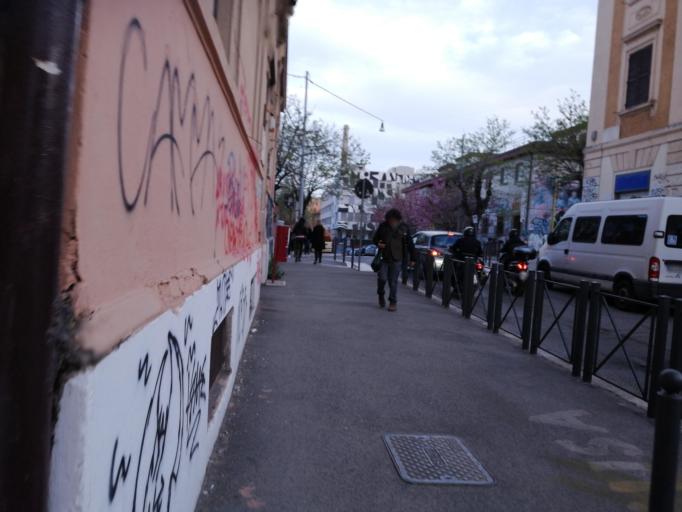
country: IT
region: Latium
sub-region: Citta metropolitana di Roma Capitale
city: Rome
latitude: 41.8977
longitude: 12.5160
